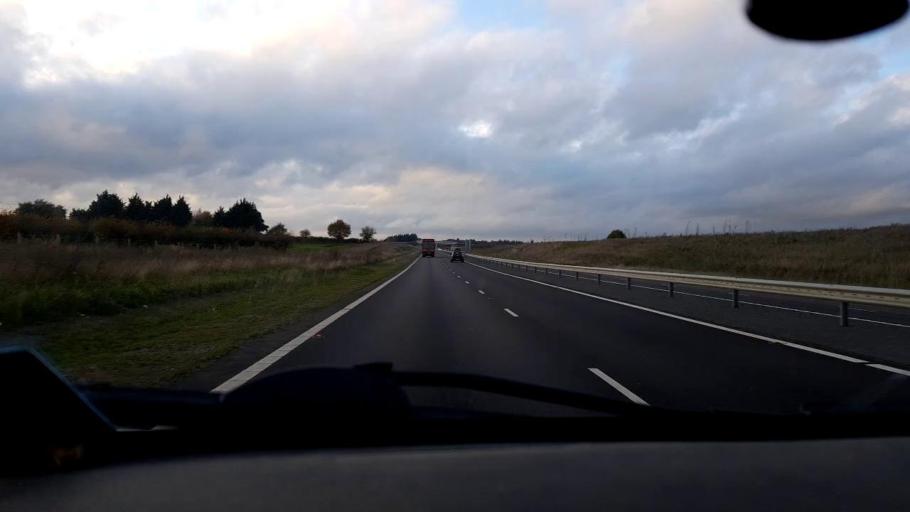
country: GB
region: England
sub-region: Norfolk
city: Horsford
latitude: 52.6897
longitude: 1.2333
